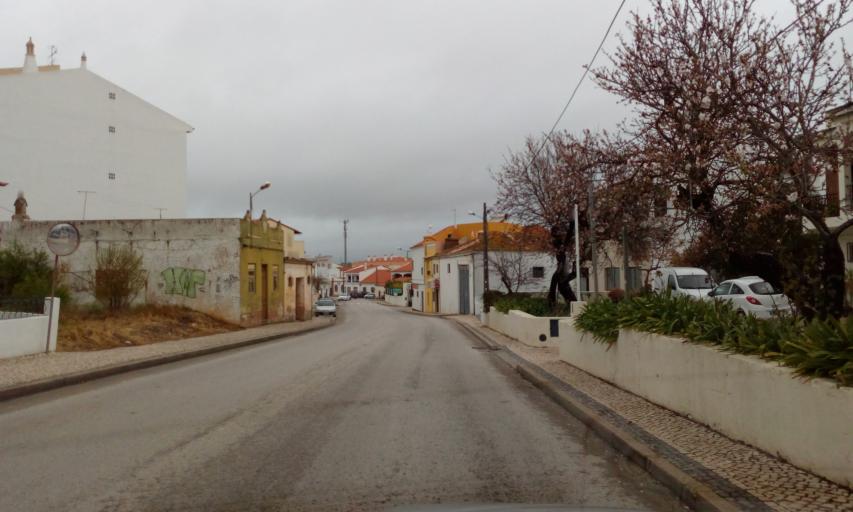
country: PT
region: Faro
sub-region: Albufeira
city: Guia
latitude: 37.1623
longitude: -8.3013
